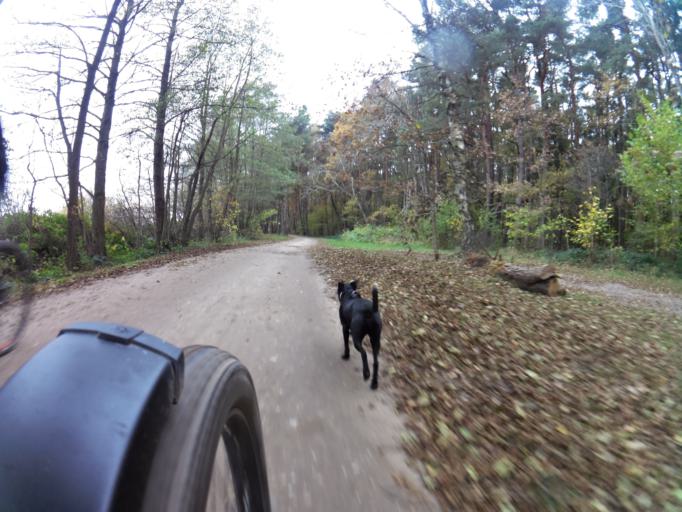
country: PL
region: Pomeranian Voivodeship
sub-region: Powiat pucki
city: Krokowa
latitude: 54.8289
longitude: 18.1300
